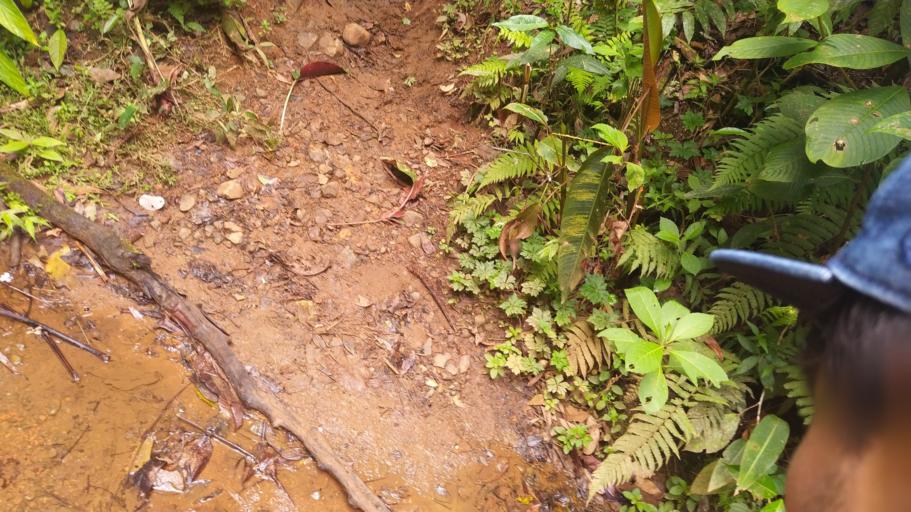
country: CO
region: Valle del Cauca
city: Cali
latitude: 3.4228
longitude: -76.6145
